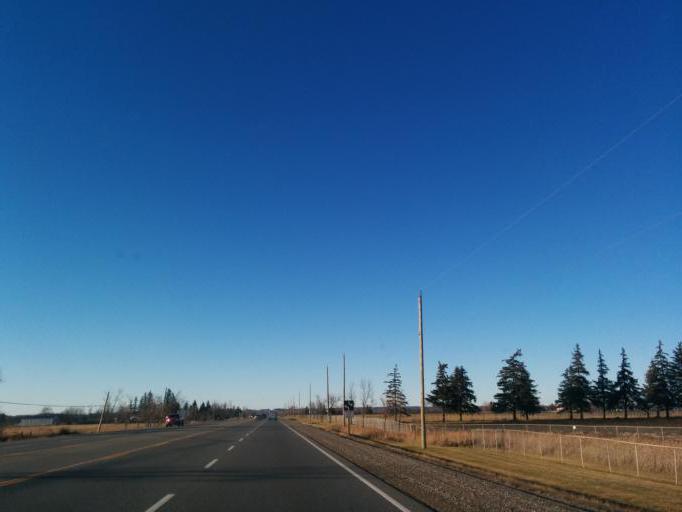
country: CA
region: Ontario
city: Brampton
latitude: 43.7784
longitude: -79.8848
